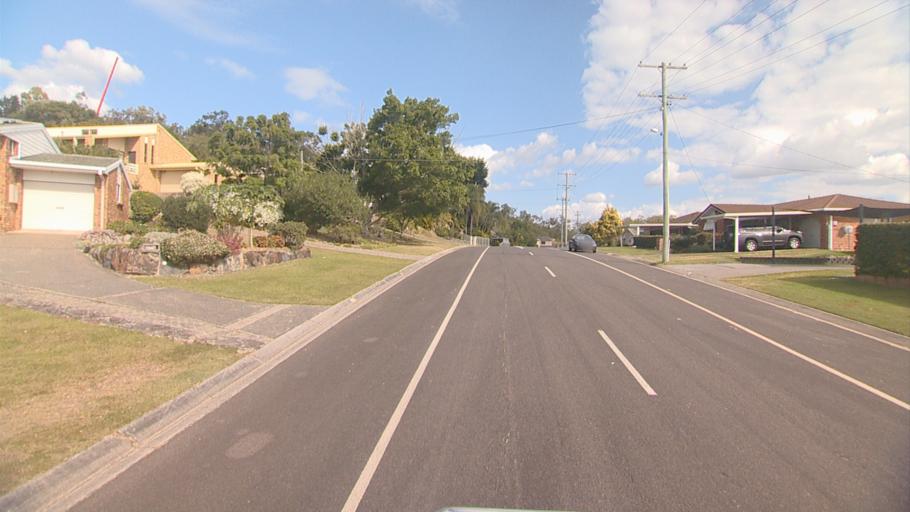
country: AU
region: Queensland
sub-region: Logan
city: Windaroo
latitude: -27.7252
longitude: 153.1971
